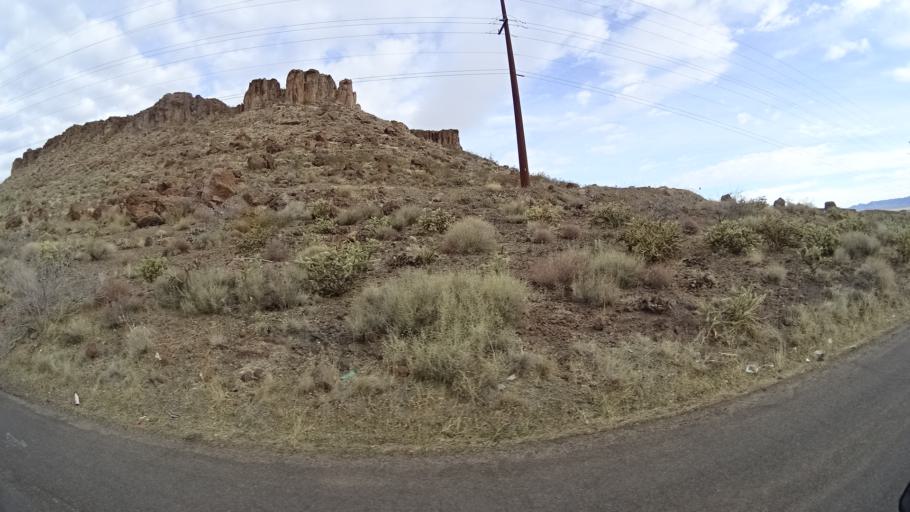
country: US
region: Arizona
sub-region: Mohave County
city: Kingman
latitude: 35.2176
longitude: -114.0617
